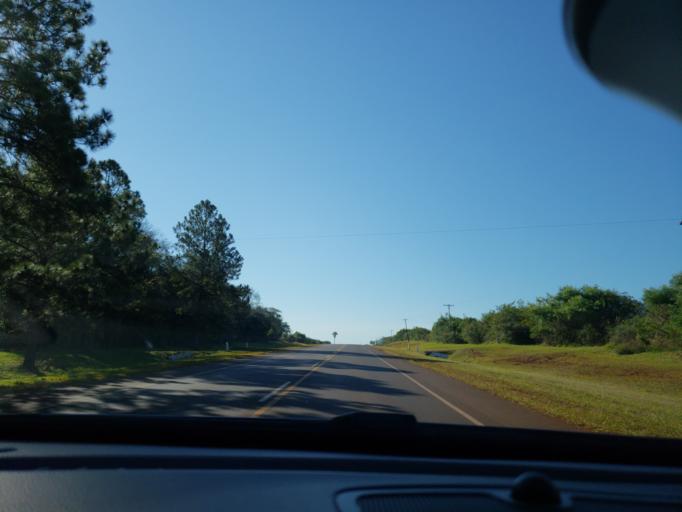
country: AR
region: Misiones
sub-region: Departamento de Apostoles
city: Apostoles
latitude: -27.8709
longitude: -55.7659
